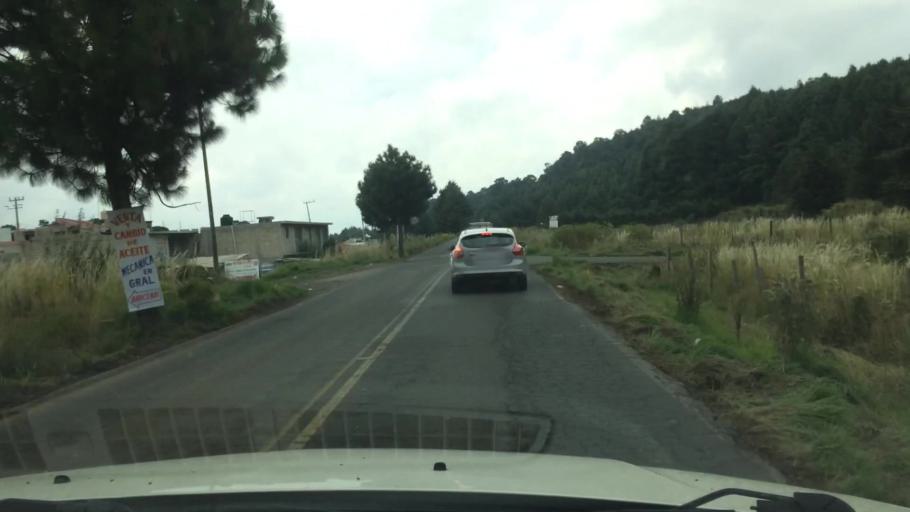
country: MX
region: Mexico City
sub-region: Tlalpan
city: Lomas de Tepemecatl
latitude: 19.2317
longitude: -99.2261
